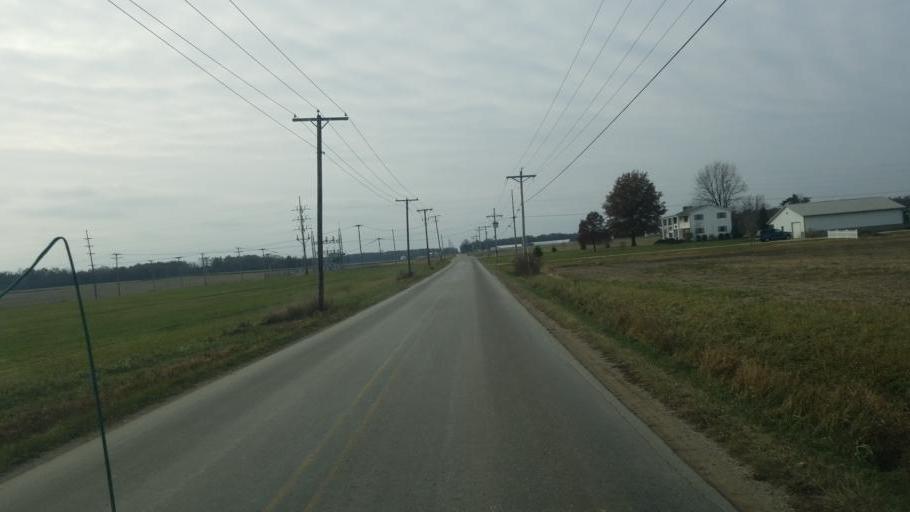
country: US
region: Indiana
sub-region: Adams County
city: Berne
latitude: 40.6430
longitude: -84.9621
